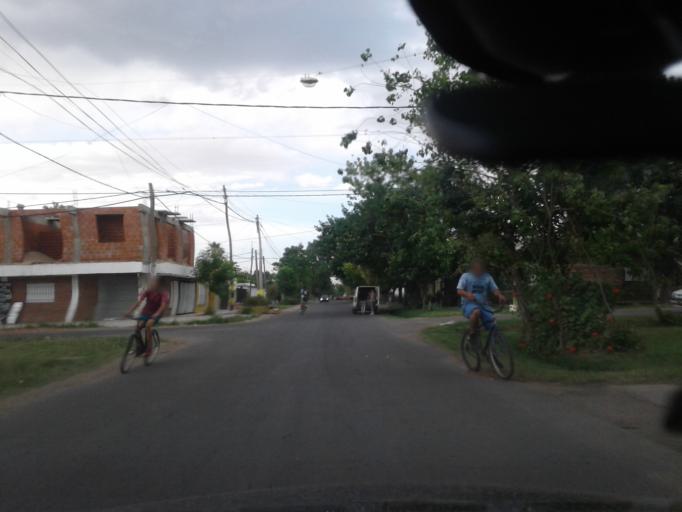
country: AR
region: Santa Fe
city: Granadero Baigorria
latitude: -32.8892
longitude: -60.7204
